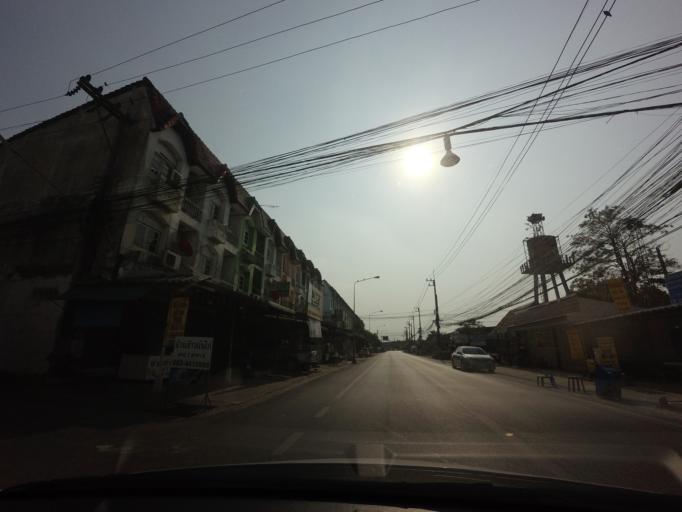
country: TH
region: Nakhon Pathom
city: Sam Phran
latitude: 13.6956
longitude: 100.2350
